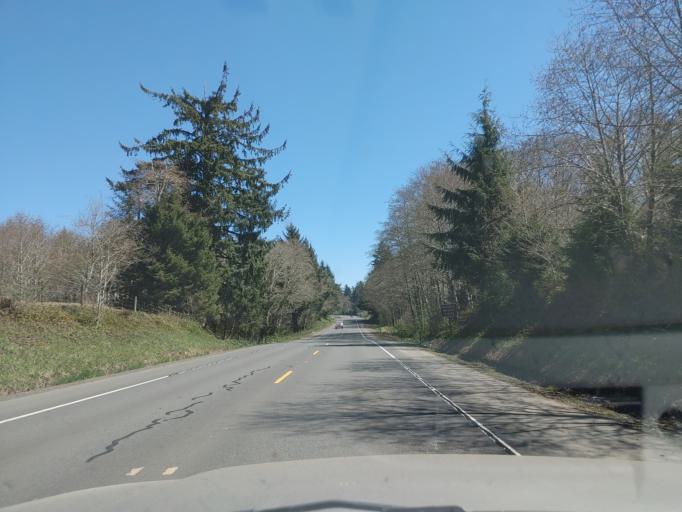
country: US
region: Oregon
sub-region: Clatsop County
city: Warrenton
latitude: 46.1432
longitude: -123.8795
